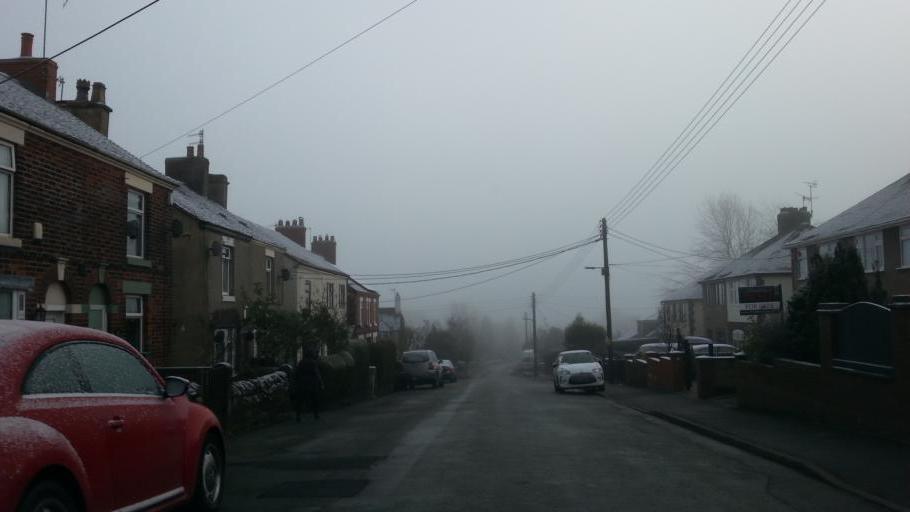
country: GB
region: England
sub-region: Staffordshire
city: Biddulph
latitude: 53.1253
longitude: -2.1779
